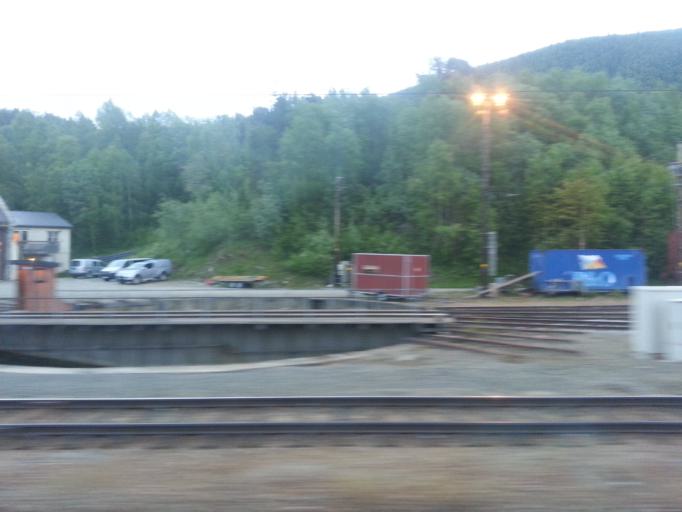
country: NO
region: Oppland
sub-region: Dovre
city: Dombas
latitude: 62.0695
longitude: 9.1264
